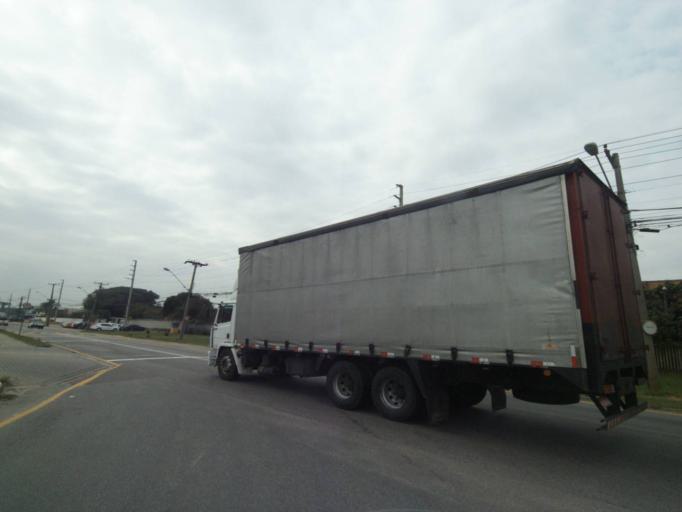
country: BR
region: Parana
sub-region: Curitiba
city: Curitiba
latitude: -25.5199
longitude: -49.3279
